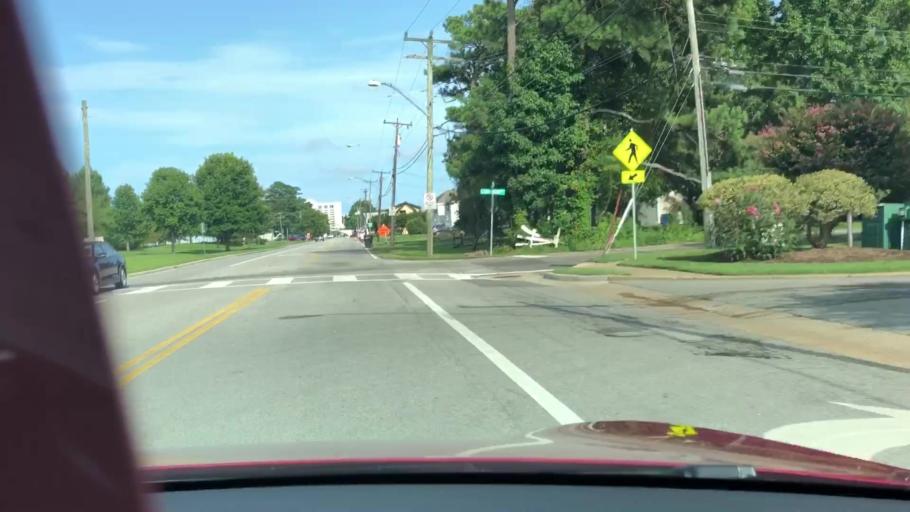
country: US
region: Virginia
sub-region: City of Virginia Beach
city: Virginia Beach
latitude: 36.8377
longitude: -75.9836
